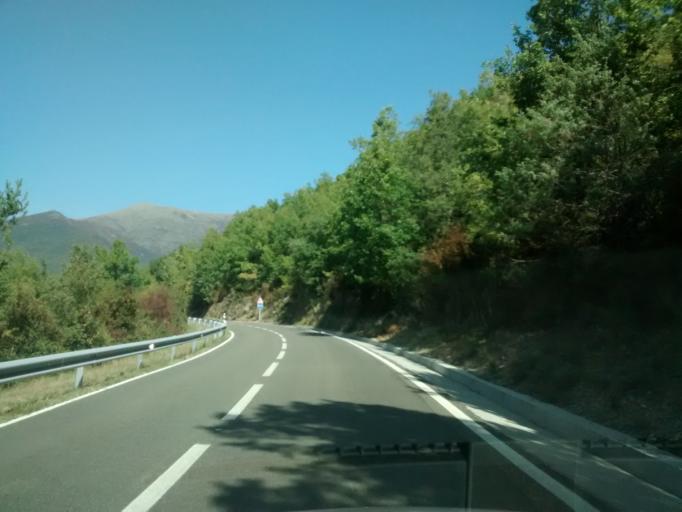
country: ES
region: Aragon
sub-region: Provincia de Huesca
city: Fiscal
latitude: 42.5158
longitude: -0.1270
